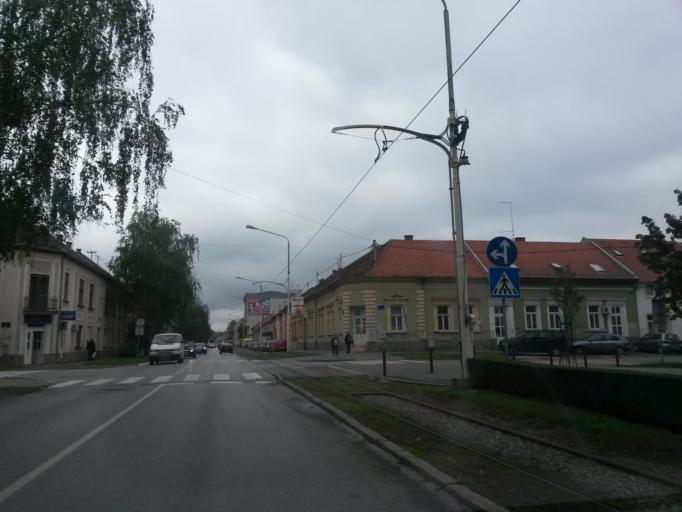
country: HR
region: Osjecko-Baranjska
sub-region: Grad Osijek
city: Osijek
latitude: 45.5548
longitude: 18.6792
